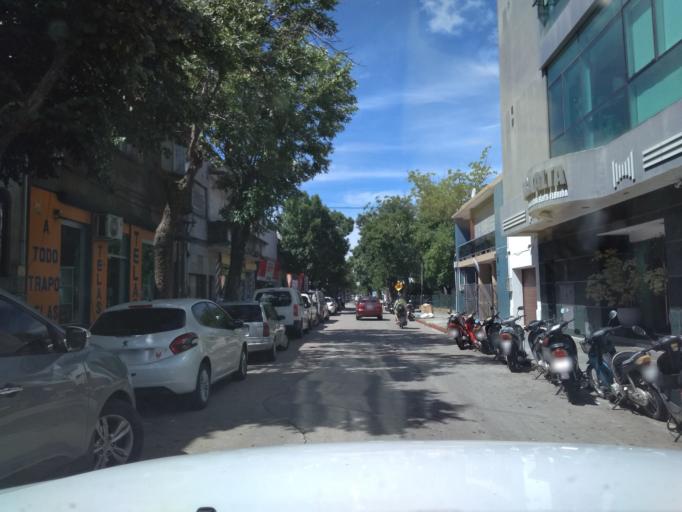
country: UY
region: Florida
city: Florida
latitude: -34.0982
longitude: -56.2155
